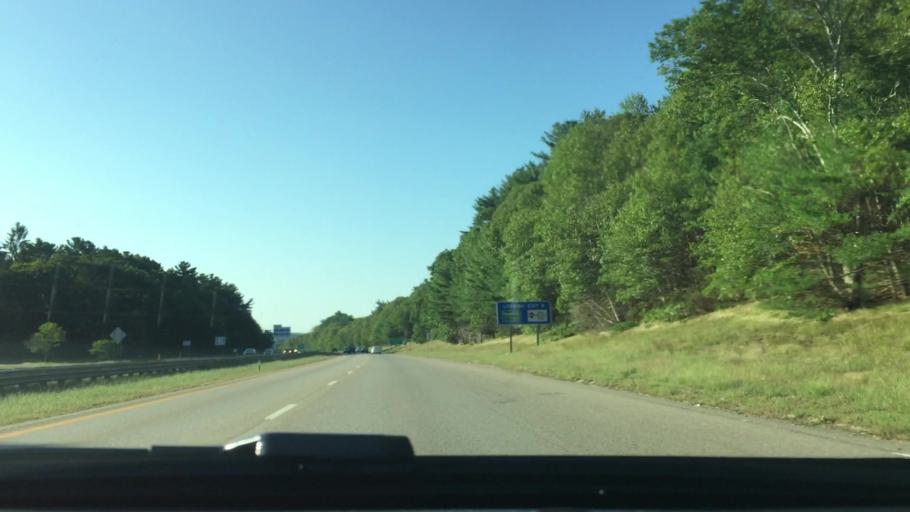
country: US
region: Massachusetts
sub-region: Plymouth County
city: Kingston
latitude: 42.0133
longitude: -70.7266
